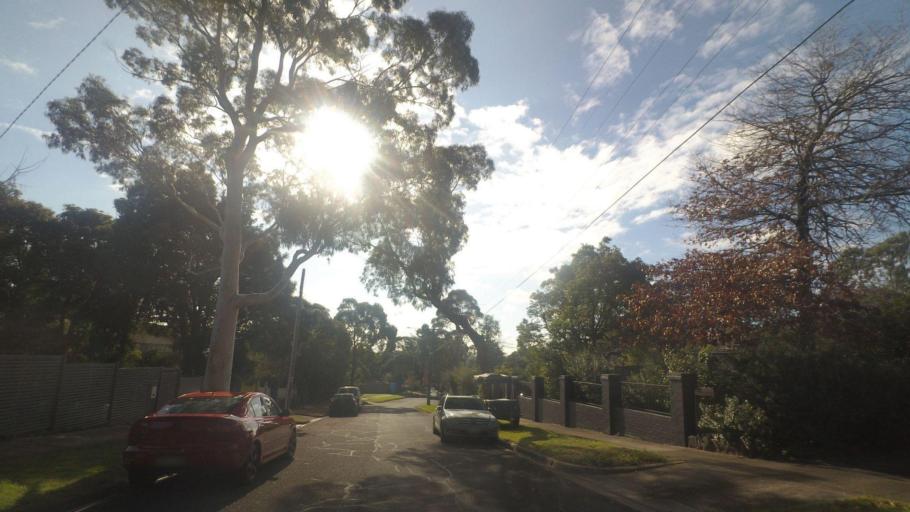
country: AU
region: Victoria
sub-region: Whitehorse
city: Mont Albert North
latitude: -37.8002
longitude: 145.1076
